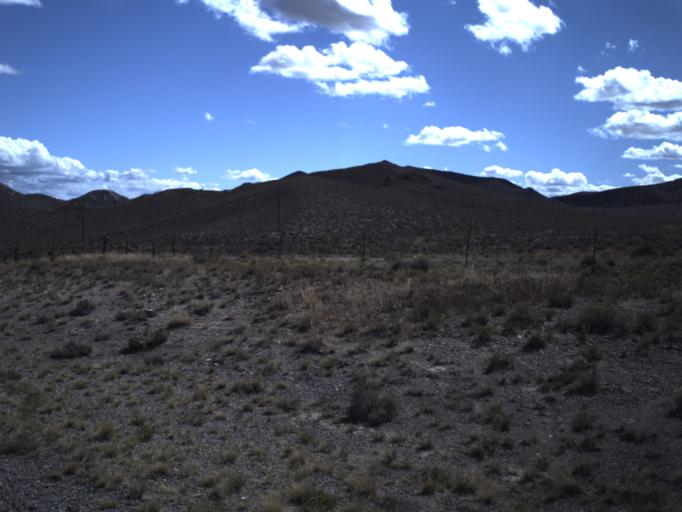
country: US
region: Utah
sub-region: Beaver County
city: Milford
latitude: 38.4249
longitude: -113.1155
